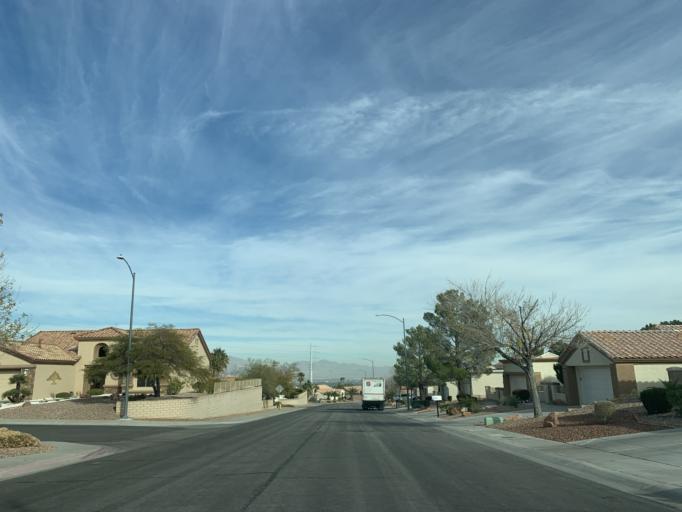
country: US
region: Nevada
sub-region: Clark County
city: Summerlin South
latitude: 36.2168
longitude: -115.3270
